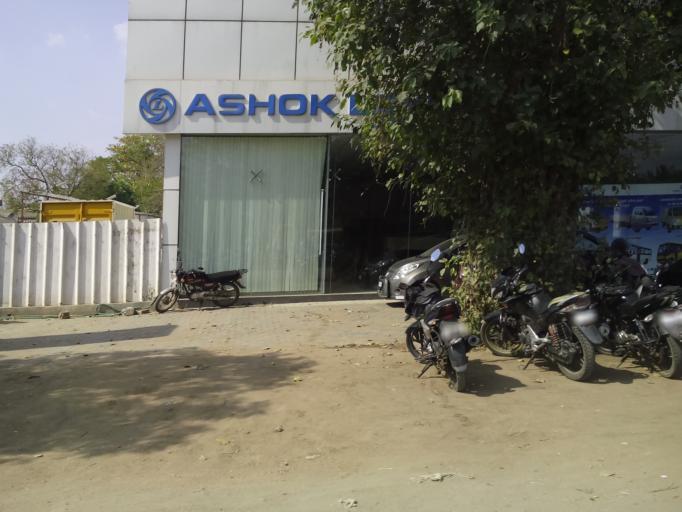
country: IN
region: Tamil Nadu
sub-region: Coimbatore
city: Singanallur
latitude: 10.9992
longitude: 77.0234
